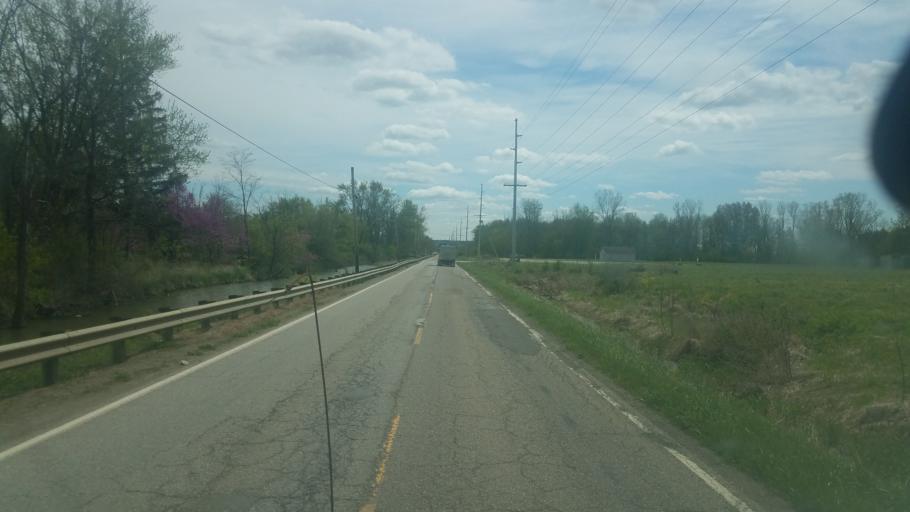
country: US
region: Ohio
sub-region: Wayne County
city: Wooster
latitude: 40.7680
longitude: -81.9443
